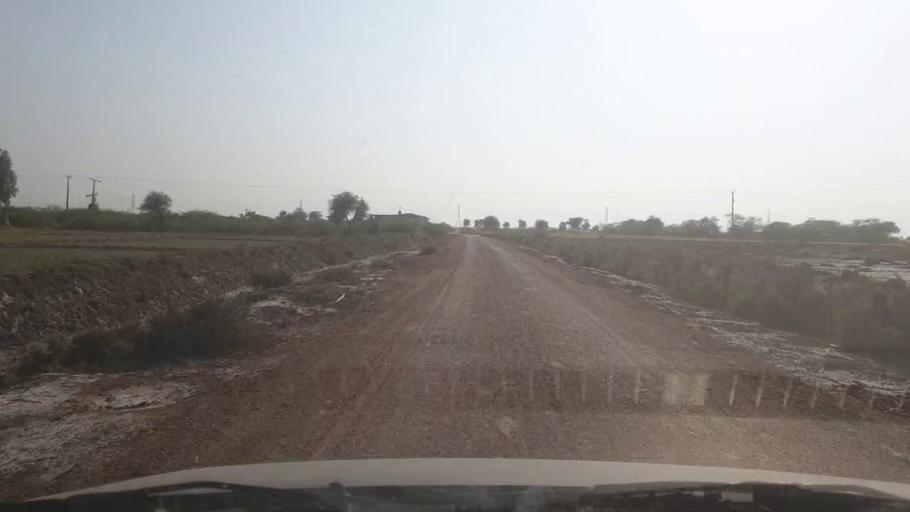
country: PK
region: Sindh
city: Samaro
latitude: 25.1410
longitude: 69.3771
